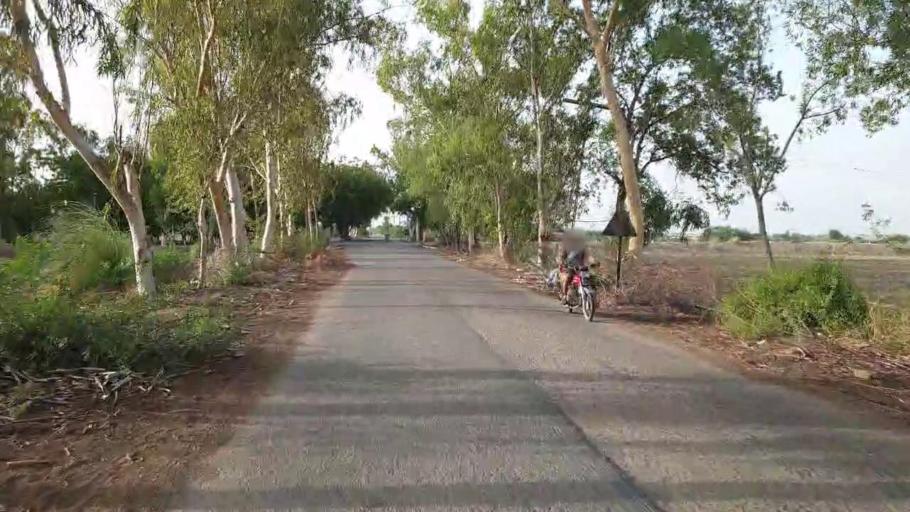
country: PK
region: Sindh
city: Bozdar
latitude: 27.1206
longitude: 68.9560
